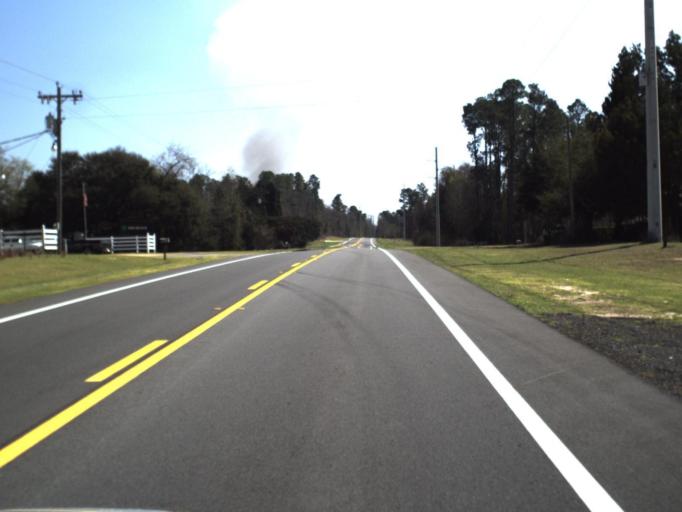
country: US
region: Florida
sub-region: Jackson County
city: Malone
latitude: 30.8349
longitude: -85.0580
